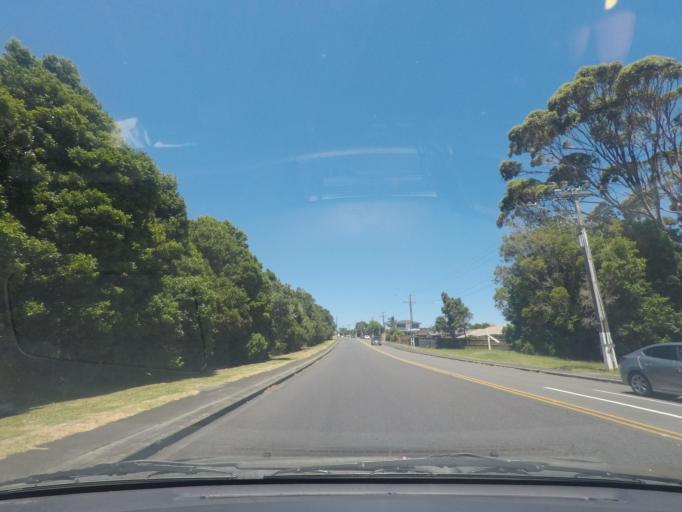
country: NZ
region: Auckland
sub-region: Auckland
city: Waitakere
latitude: -36.9260
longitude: 174.7248
